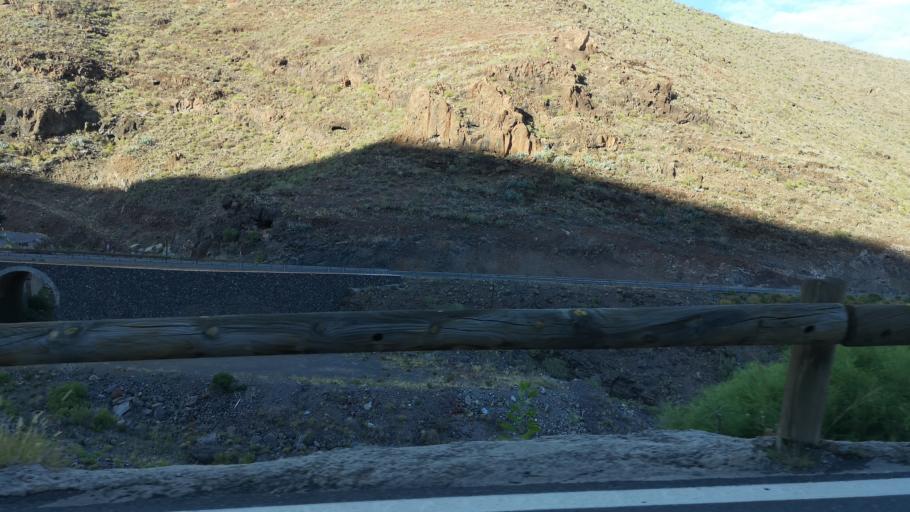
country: ES
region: Canary Islands
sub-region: Provincia de Santa Cruz de Tenerife
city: San Sebastian de la Gomera
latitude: 28.0861
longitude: -17.1299
